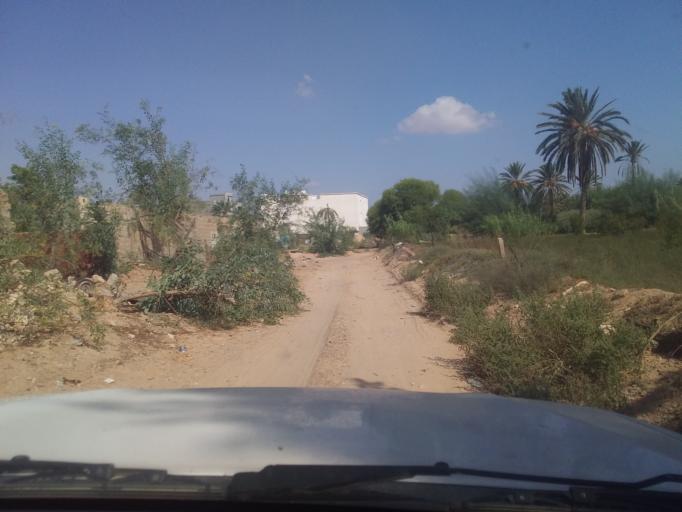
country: TN
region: Qabis
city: Gabes
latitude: 33.6275
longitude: 10.2822
